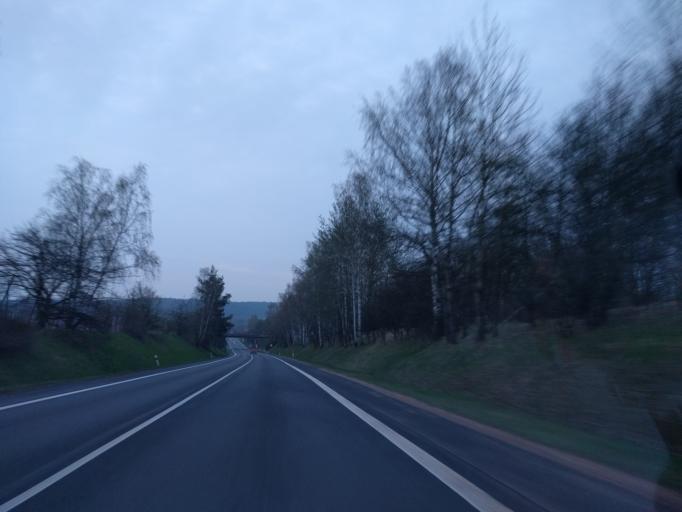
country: CZ
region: Ustecky
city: Kryry
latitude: 50.1363
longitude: 13.4307
